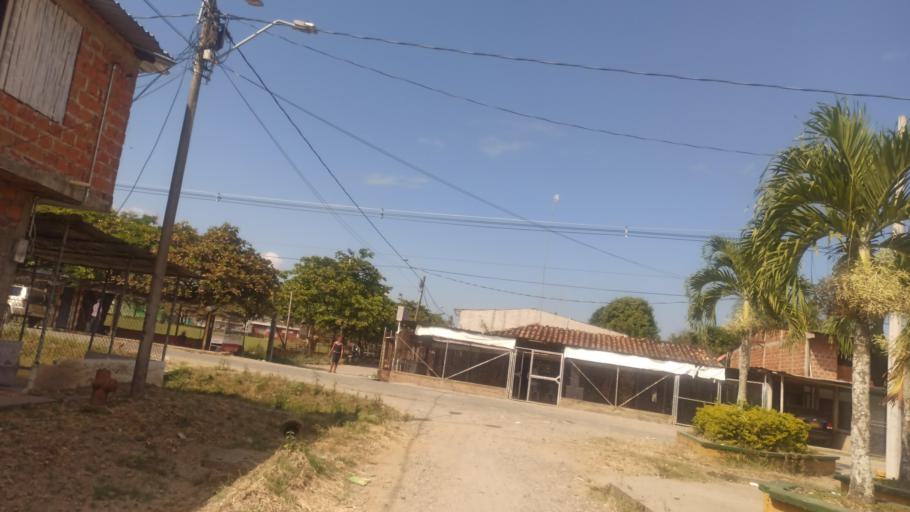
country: CO
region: Valle del Cauca
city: Jamundi
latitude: 3.1288
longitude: -76.5563
